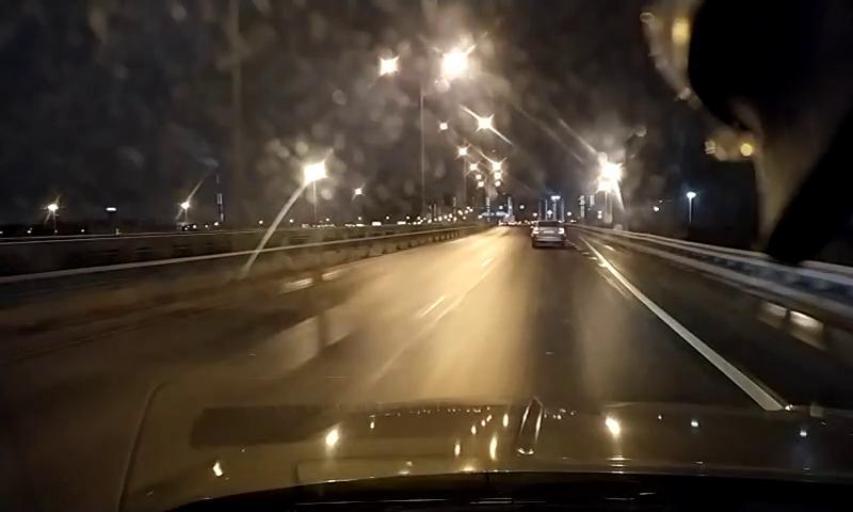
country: RU
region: Leningrad
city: Bugry
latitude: 60.0937
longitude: 30.3721
